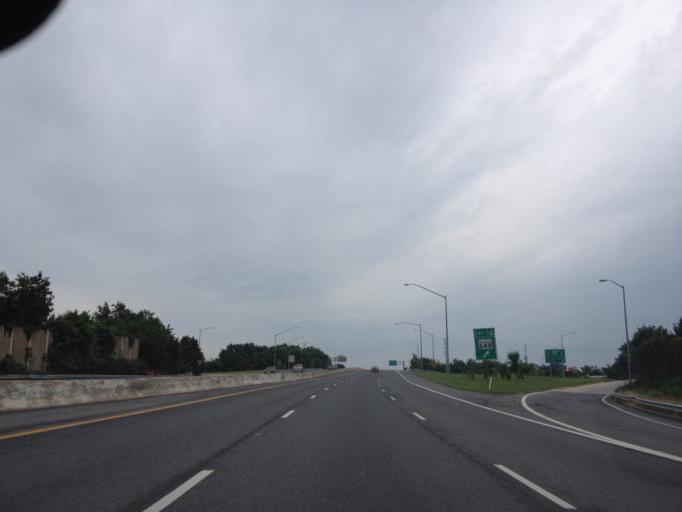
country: US
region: Maryland
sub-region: Anne Arundel County
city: Ferndale
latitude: 39.1792
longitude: -76.6345
